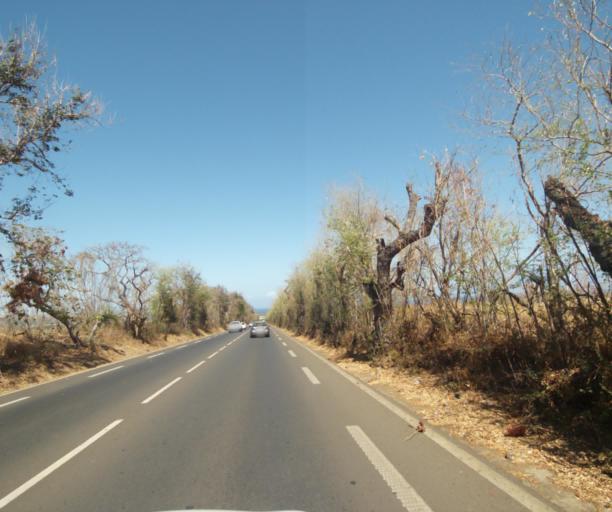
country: RE
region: Reunion
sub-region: Reunion
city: Le Port
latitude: -20.9813
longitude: 55.3123
